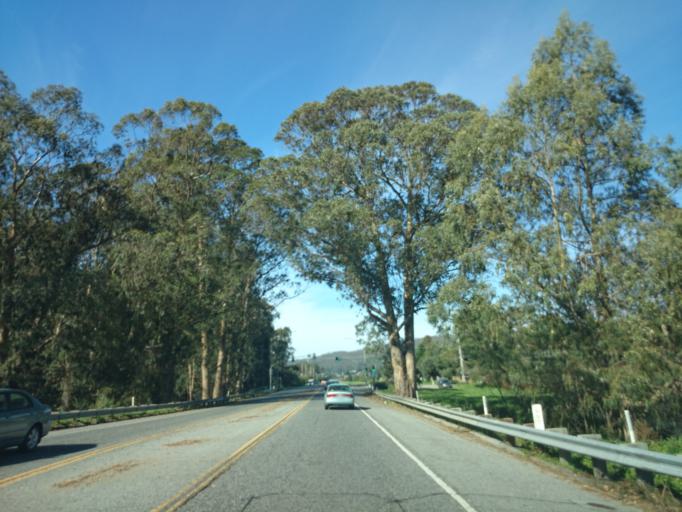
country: US
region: California
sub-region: San Mateo County
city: Half Moon Bay
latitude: 37.4824
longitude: -122.4456
